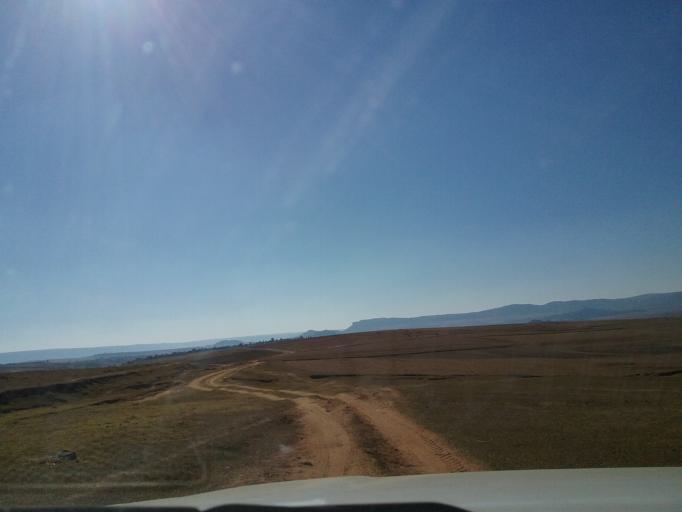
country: LS
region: Maseru
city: Nako
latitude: -29.4978
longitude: 27.5980
